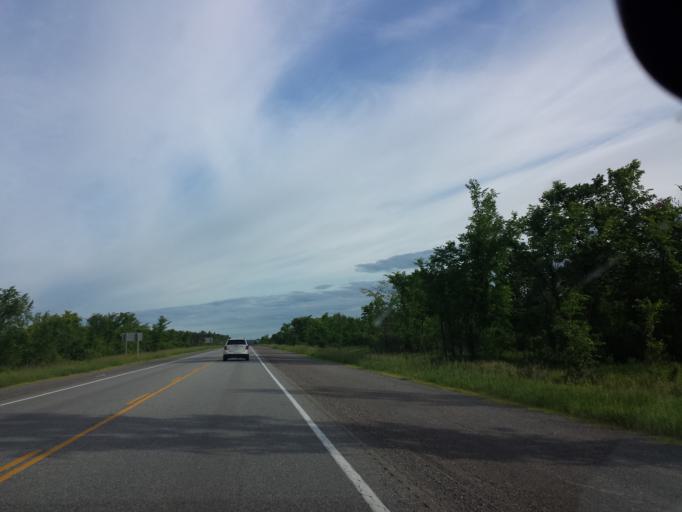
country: CA
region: Ontario
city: Renfrew
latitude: 45.4629
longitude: -76.6163
